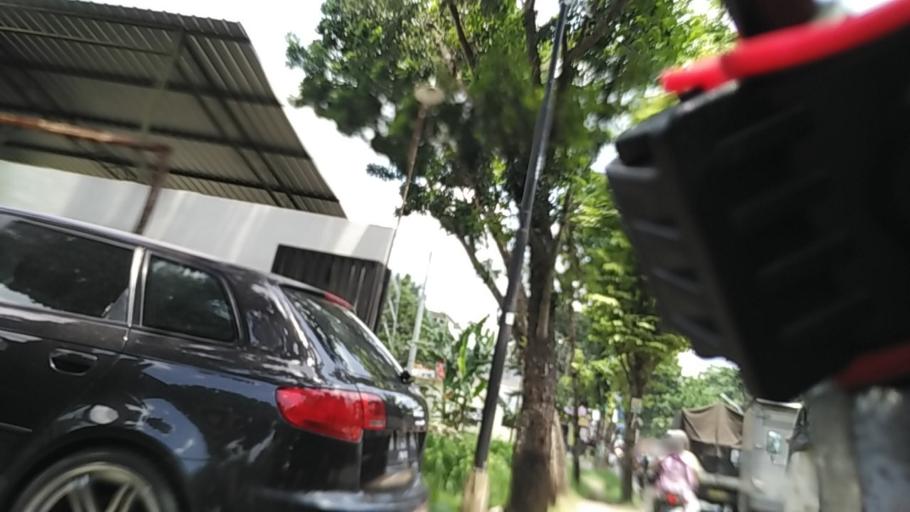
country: ID
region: Central Java
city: Semarang
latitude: -7.0132
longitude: 110.3753
